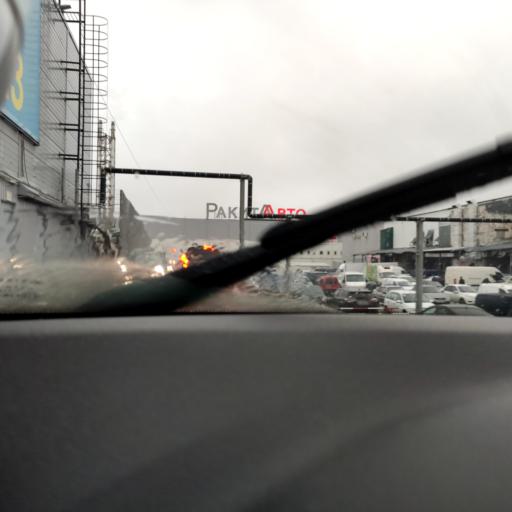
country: RU
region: Samara
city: Petra-Dubrava
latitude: 53.2768
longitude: 50.2735
